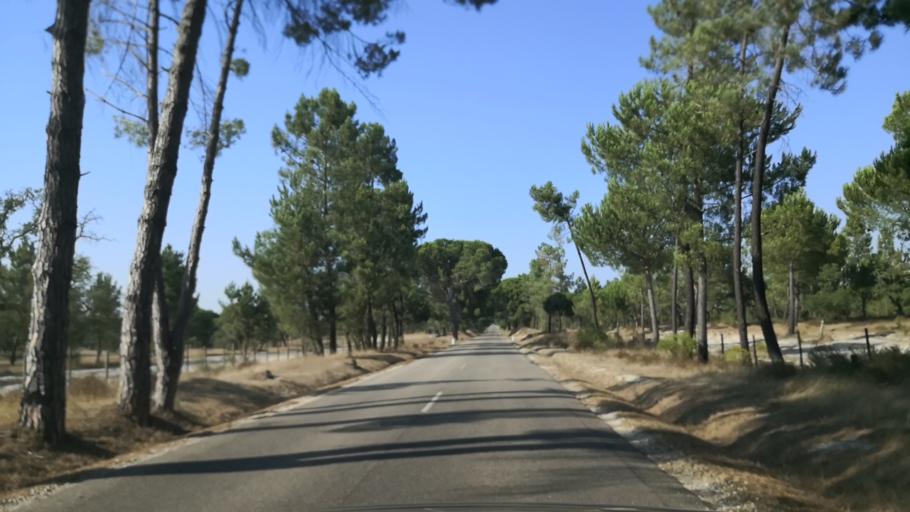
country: PT
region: Santarem
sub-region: Coruche
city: Coruche
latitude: 38.9072
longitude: -8.5270
